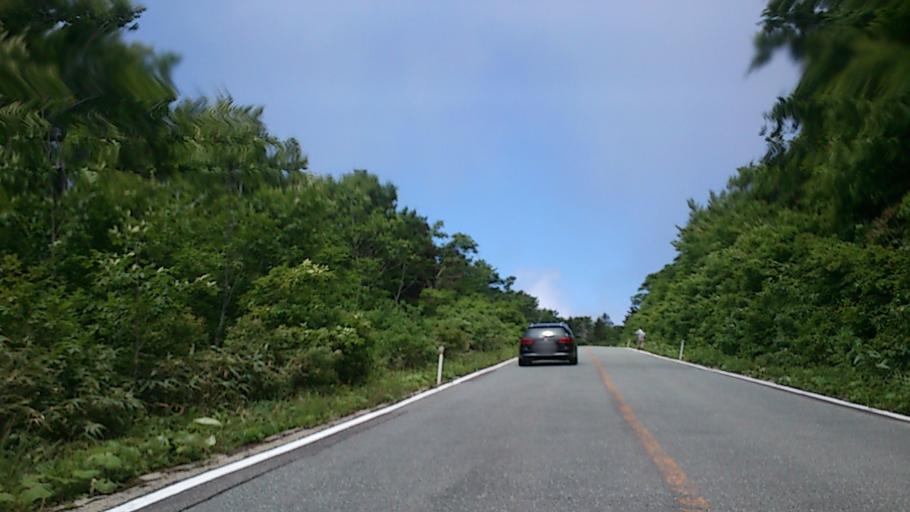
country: JP
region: Yamagata
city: Yamagata-shi
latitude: 38.1180
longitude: 140.4217
